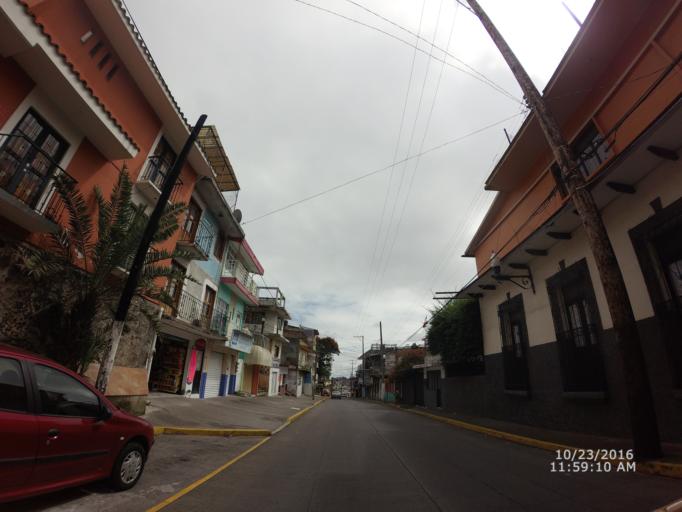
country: MX
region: Veracruz
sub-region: Xalapa
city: Xalapa de Enriquez
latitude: 19.5330
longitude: -96.9184
